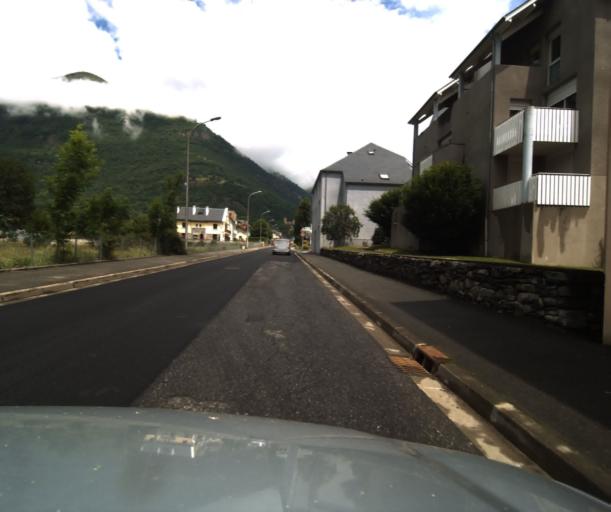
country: FR
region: Midi-Pyrenees
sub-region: Departement des Hautes-Pyrenees
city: Luz-Saint-Sauveur
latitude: 42.8702
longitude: -0.0083
